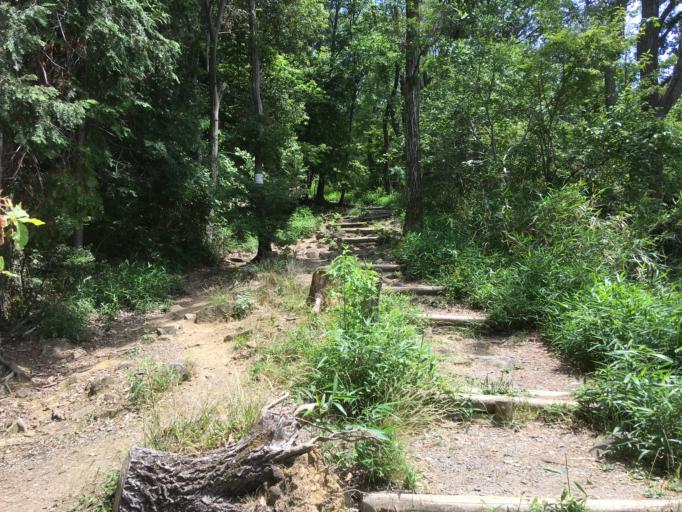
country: JP
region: Nara
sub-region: Ikoma-shi
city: Ikoma
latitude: 34.6661
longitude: 135.6608
